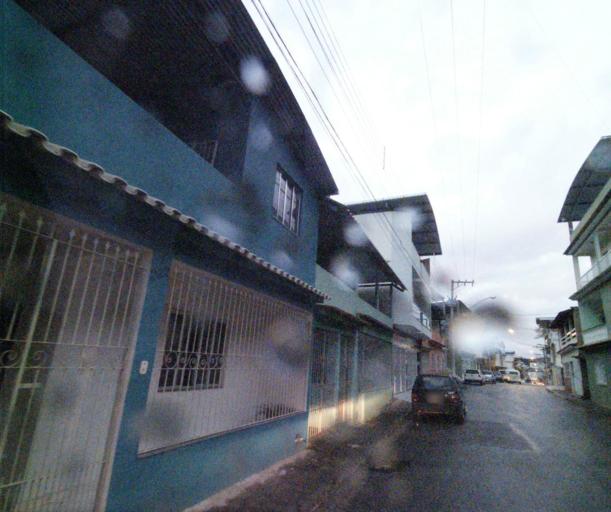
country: BR
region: Espirito Santo
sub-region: Muniz Freire
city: Muniz Freire
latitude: -20.4678
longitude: -41.4140
